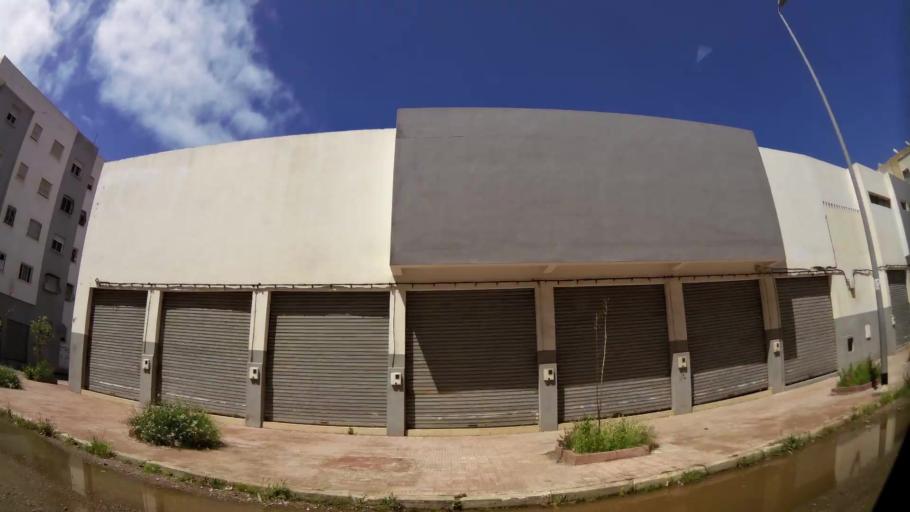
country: MA
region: Grand Casablanca
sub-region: Mediouna
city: Tit Mellil
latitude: 33.5997
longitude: -7.4804
